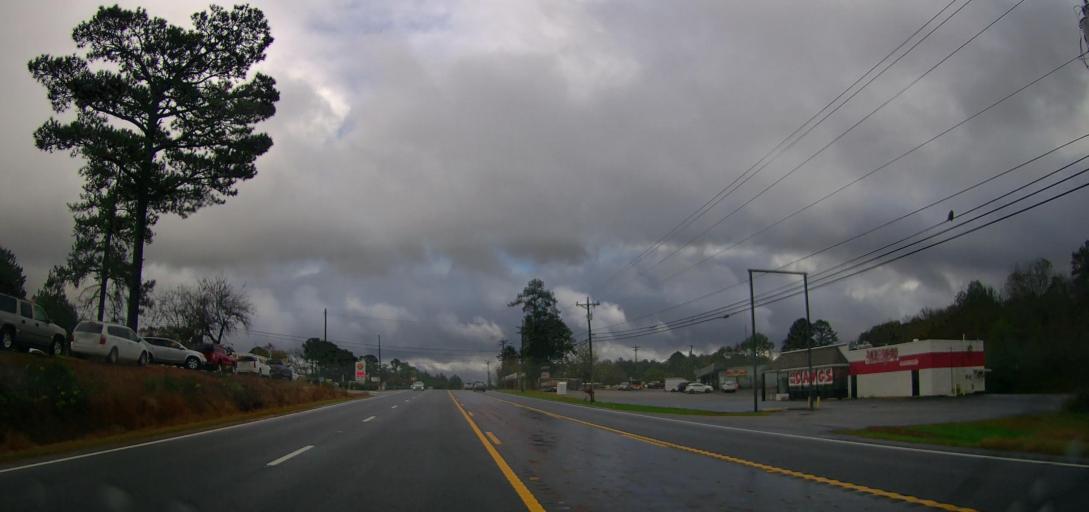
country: US
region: Georgia
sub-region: Clarke County
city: Country Club Estates
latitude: 33.9957
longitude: -83.3810
